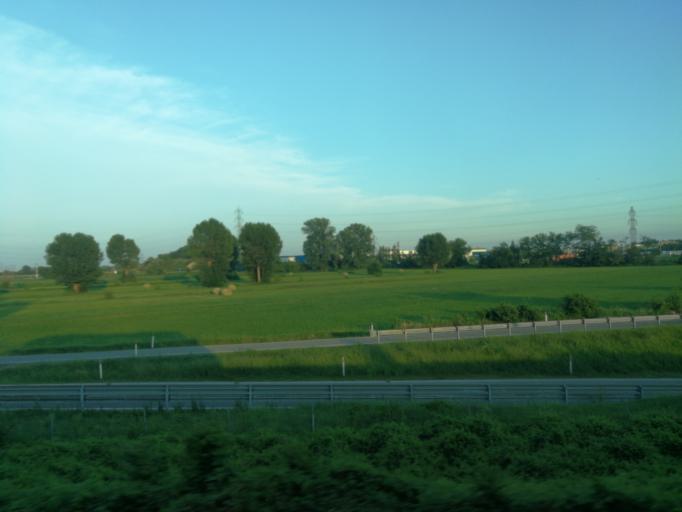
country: IT
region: Lombardy
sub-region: Citta metropolitana di Milano
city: Carugate
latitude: 45.5634
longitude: 9.3354
